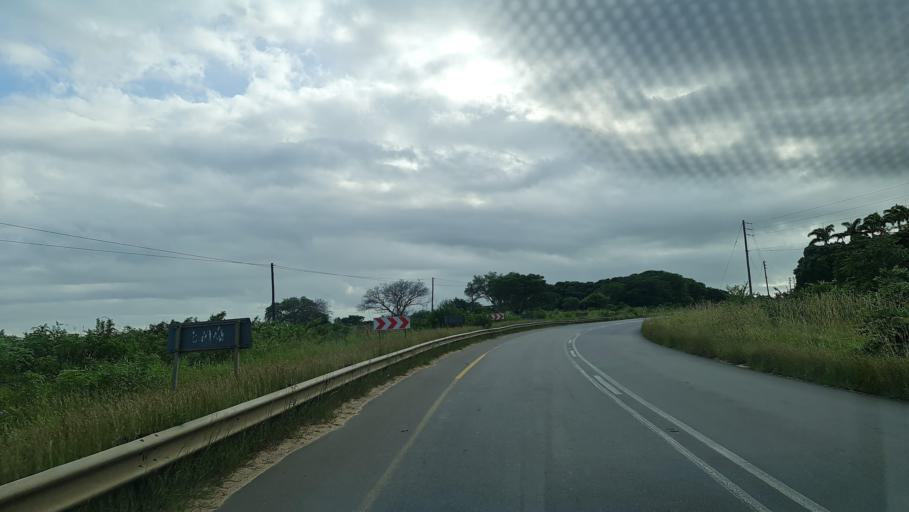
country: MZ
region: Maputo
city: Manhica
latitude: -25.4108
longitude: 32.7445
